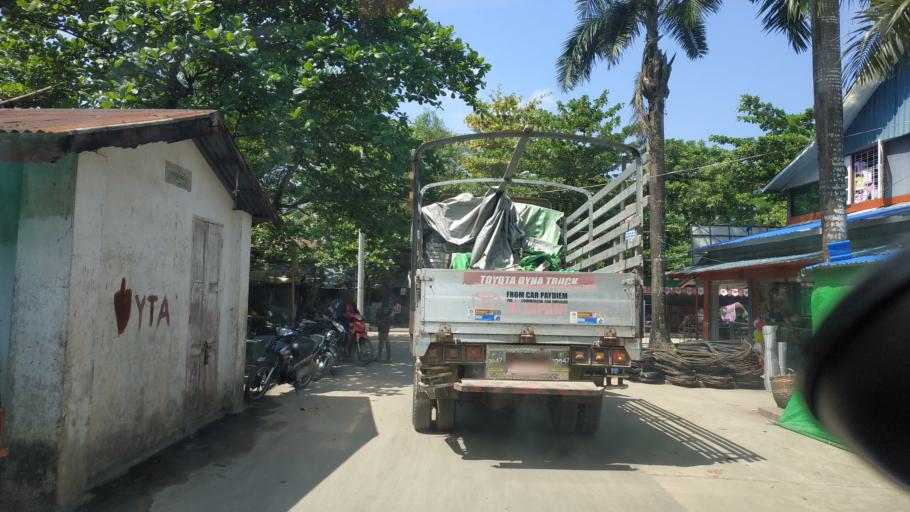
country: MM
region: Ayeyarwady
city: Mawlamyinegyunn
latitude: 16.3782
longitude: 95.2646
